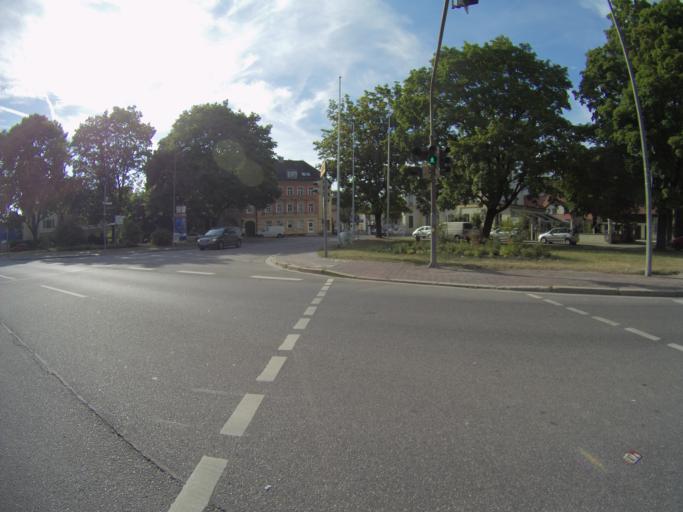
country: DE
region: Bavaria
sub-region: Upper Bavaria
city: Freising
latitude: 48.3968
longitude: 11.7447
